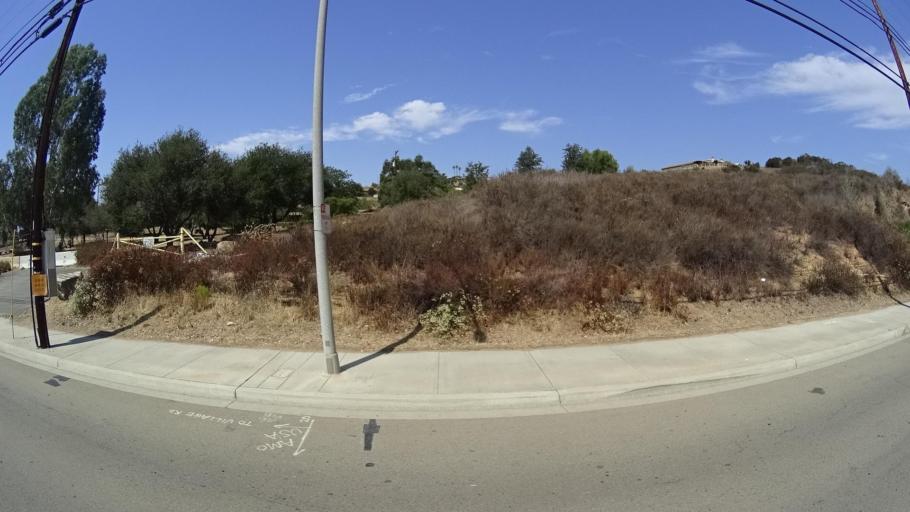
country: US
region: California
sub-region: San Diego County
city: Escondido
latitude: 33.1644
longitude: -117.0919
